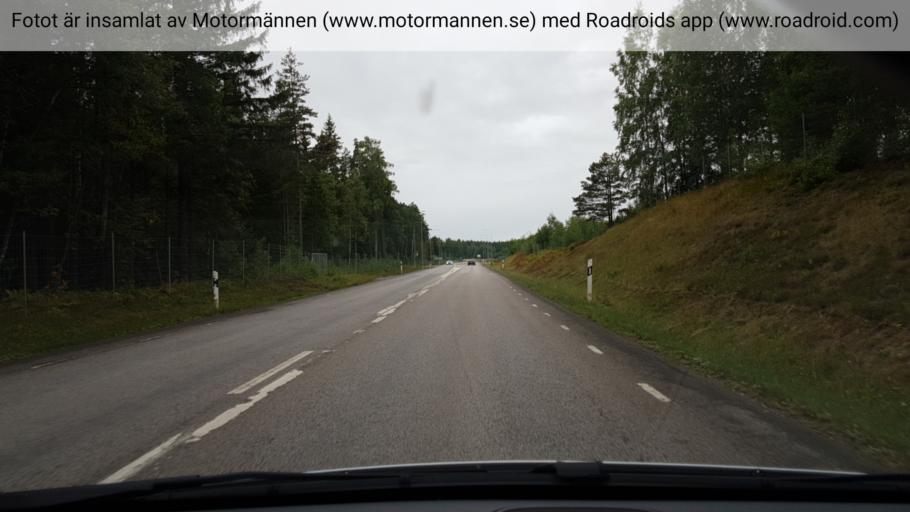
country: SE
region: Vaestra Goetaland
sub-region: Tibro Kommun
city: Tibro
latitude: 58.4470
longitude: 14.1908
